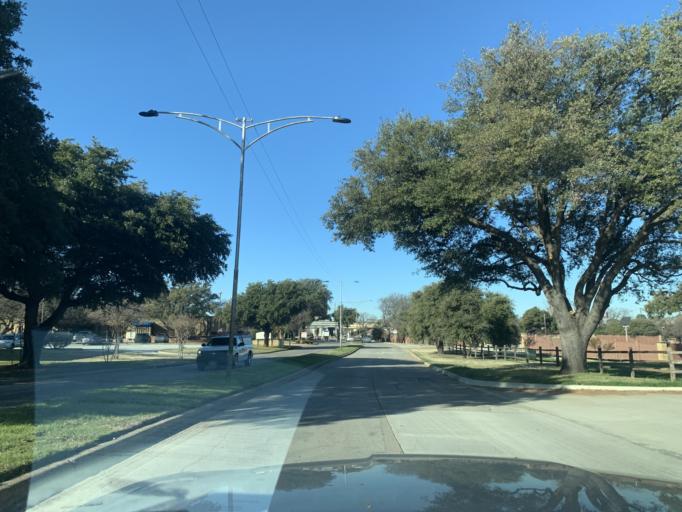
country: US
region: Texas
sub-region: Tarrant County
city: Arlington
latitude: 32.7618
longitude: -97.0601
